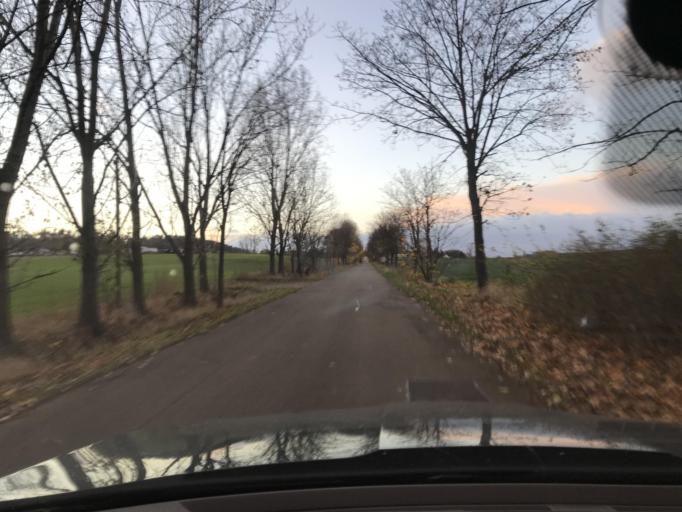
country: DE
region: Saxony-Anhalt
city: Langenstein
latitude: 51.8490
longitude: 11.0093
